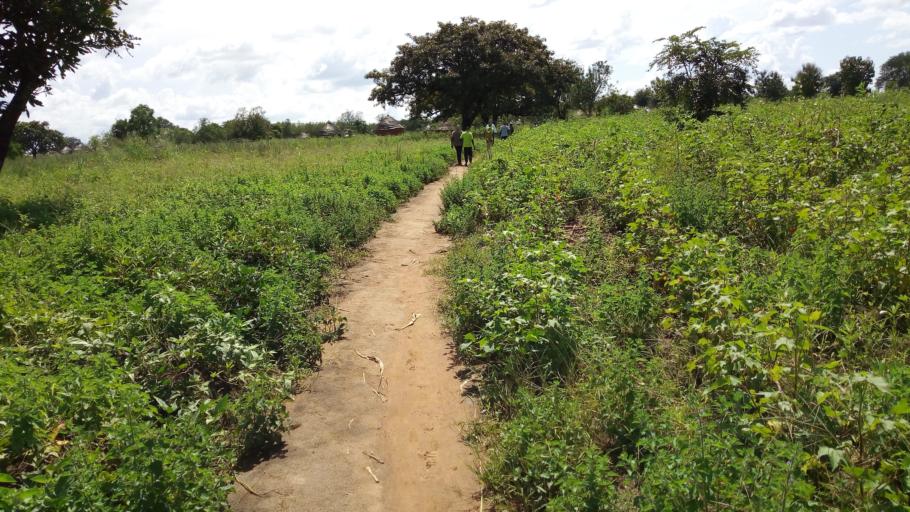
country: UG
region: Northern Region
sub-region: Adjumani District
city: Adjumani
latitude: 3.4610
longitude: 31.8971
